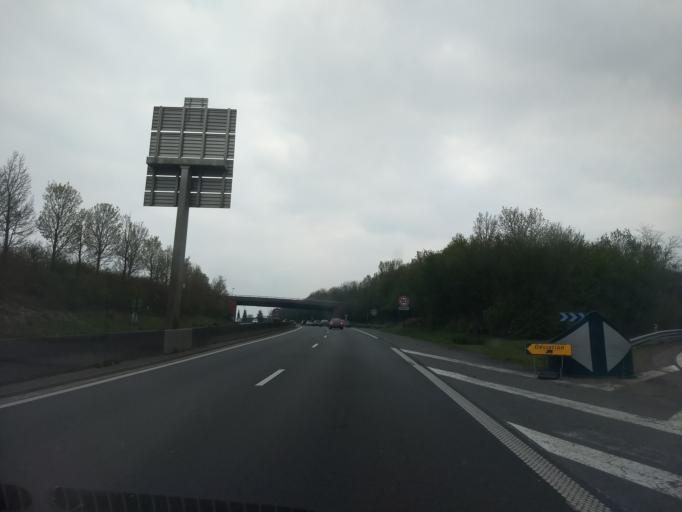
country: FR
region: Nord-Pas-de-Calais
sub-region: Departement du Pas-de-Calais
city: Saint-Nicolas
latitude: 50.3122
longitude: 2.7763
